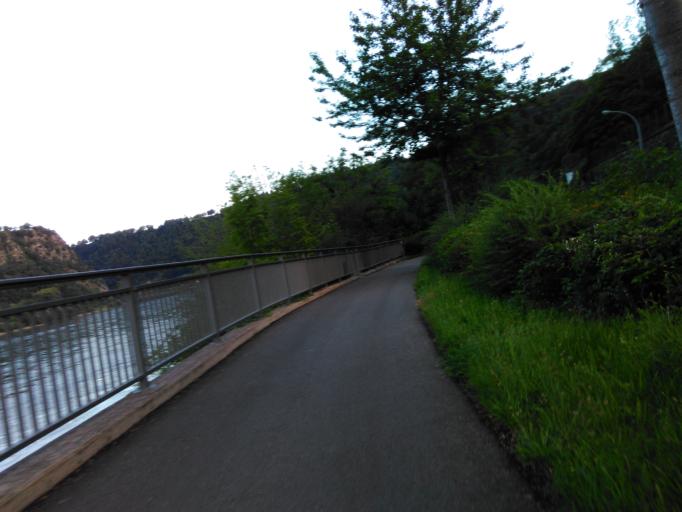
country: DE
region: Rheinland-Pfalz
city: Sankt Goarshausen
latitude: 50.1472
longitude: 7.7230
